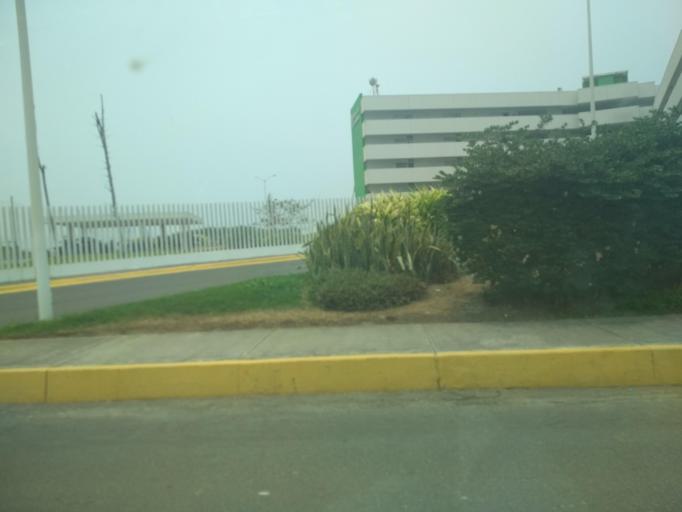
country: MX
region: Veracruz
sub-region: Alvarado
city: Playa de la Libertad
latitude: 19.0575
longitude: -96.0676
